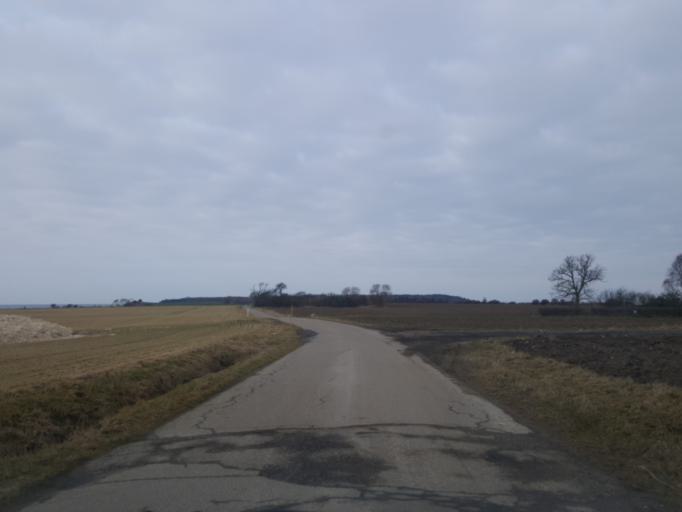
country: DK
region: Zealand
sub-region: Vordingborg Kommune
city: Neder Vindinge
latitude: 55.0478
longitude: 11.7841
